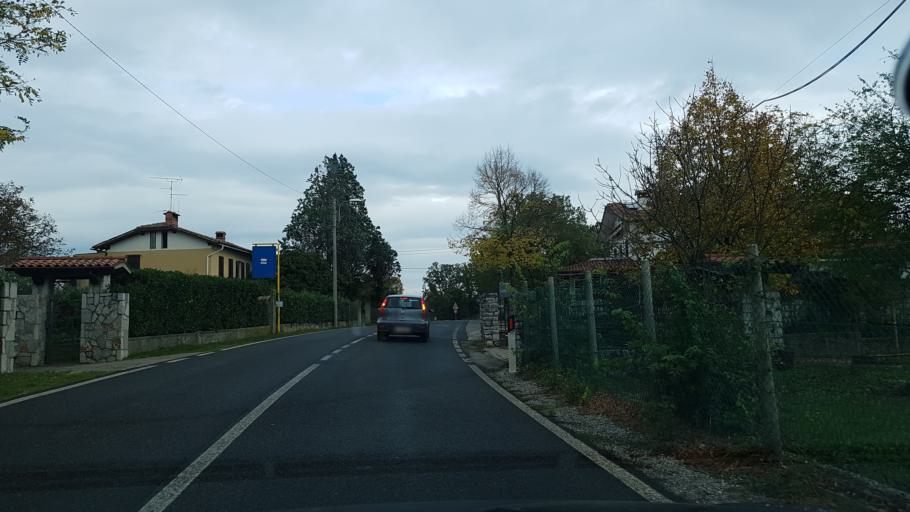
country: IT
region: Friuli Venezia Giulia
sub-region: Provincia di Gorizia
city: Doberdo del Lago
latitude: 45.8595
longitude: 13.5515
